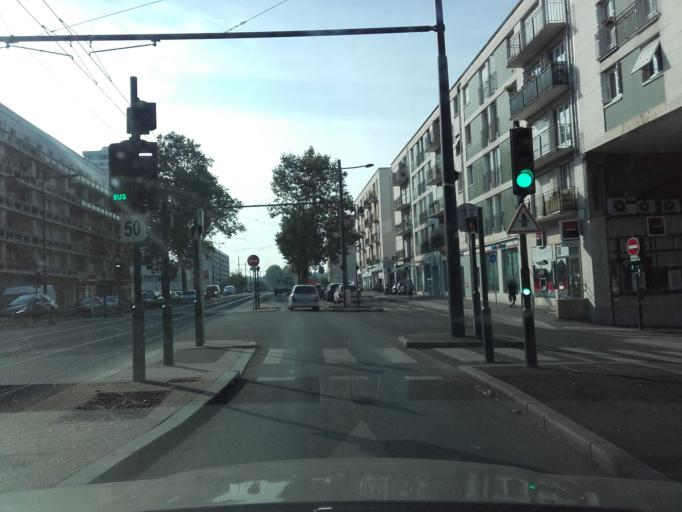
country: FR
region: Centre
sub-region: Departement d'Indre-et-Loire
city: Tours
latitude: 47.3761
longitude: 0.6945
